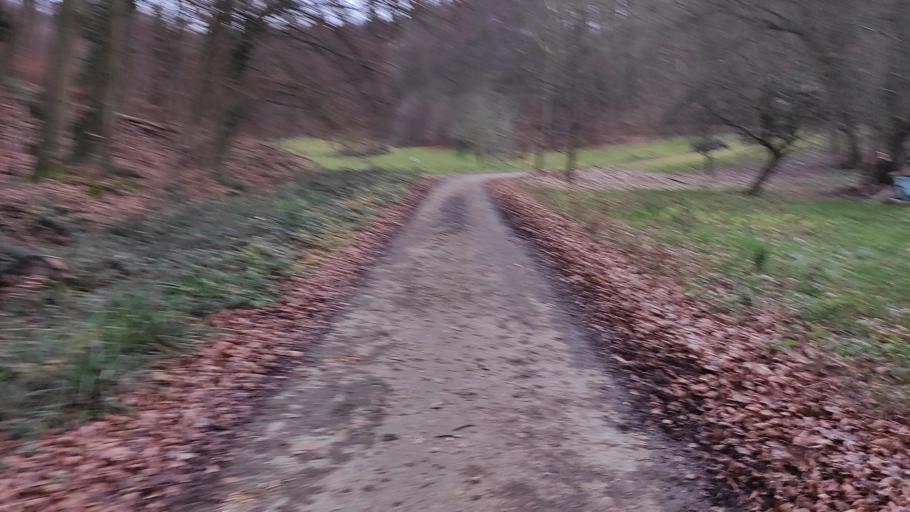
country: DE
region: Baden-Wuerttemberg
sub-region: Freiburg Region
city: Ebringen
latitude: 47.9476
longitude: 7.7746
